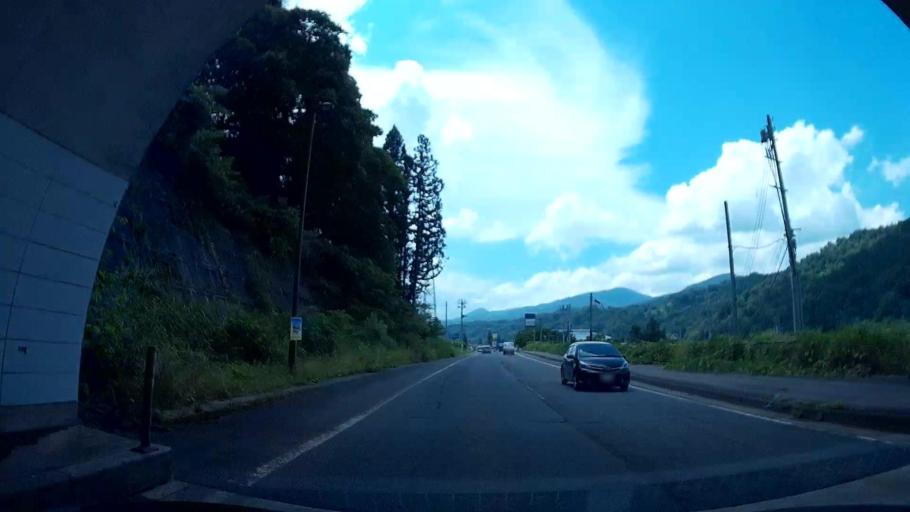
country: JP
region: Niigata
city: Tokamachi
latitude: 37.0028
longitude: 138.6379
